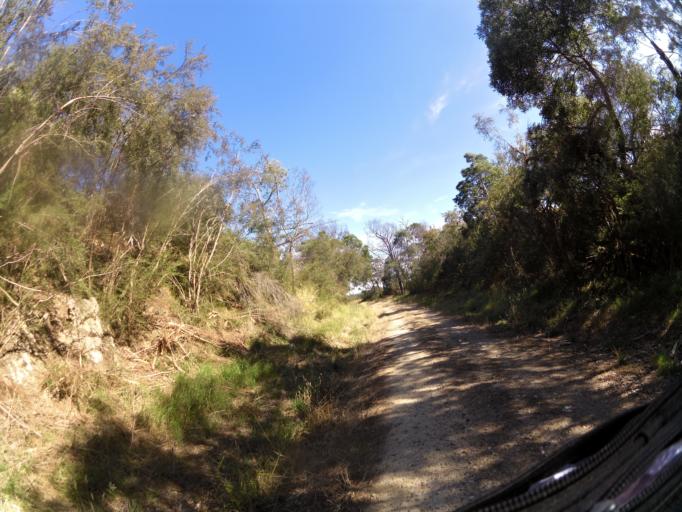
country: AU
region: Victoria
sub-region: East Gippsland
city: Lakes Entrance
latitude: -37.7391
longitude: 148.1689
